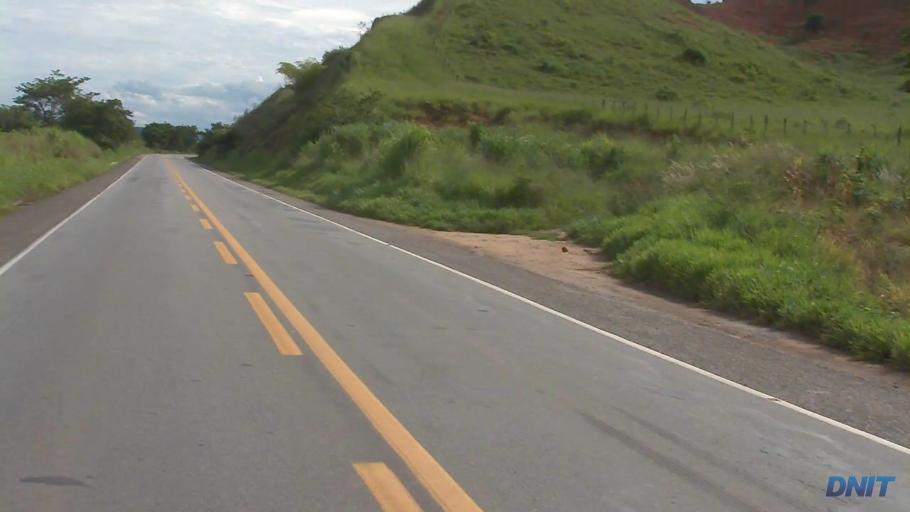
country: BR
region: Minas Gerais
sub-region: Belo Oriente
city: Belo Oriente
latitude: -19.1790
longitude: -42.2585
